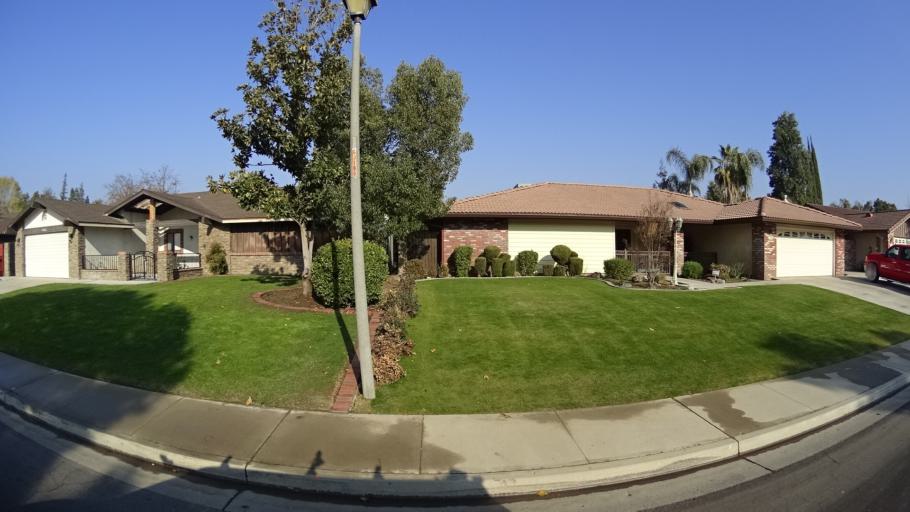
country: US
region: California
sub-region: Kern County
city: Greenacres
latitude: 35.3400
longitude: -119.0803
